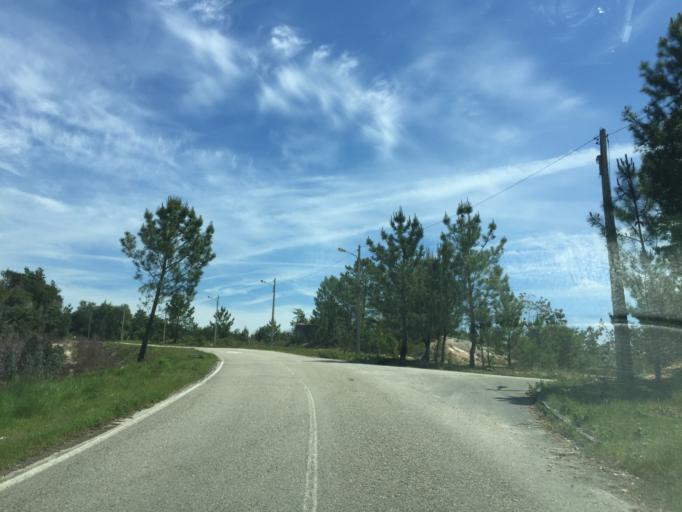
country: PT
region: Coimbra
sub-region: Soure
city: Soure
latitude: 40.0610
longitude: -8.6924
